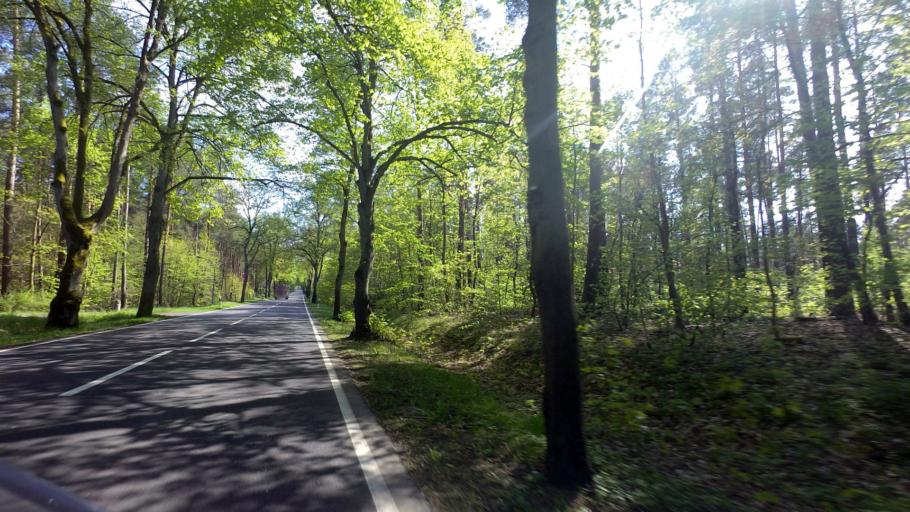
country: DE
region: Brandenburg
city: Milmersdorf
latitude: 53.0434
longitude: 13.6033
